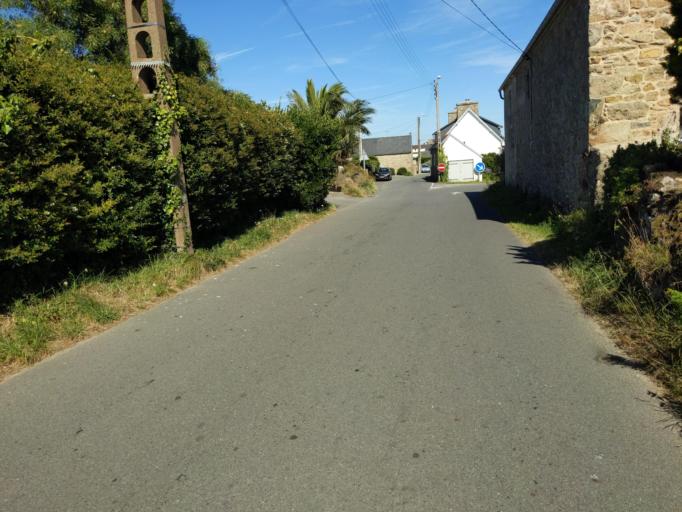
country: FR
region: Brittany
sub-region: Departement des Cotes-d'Armor
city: Pleubian
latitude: 48.8639
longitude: -3.0885
